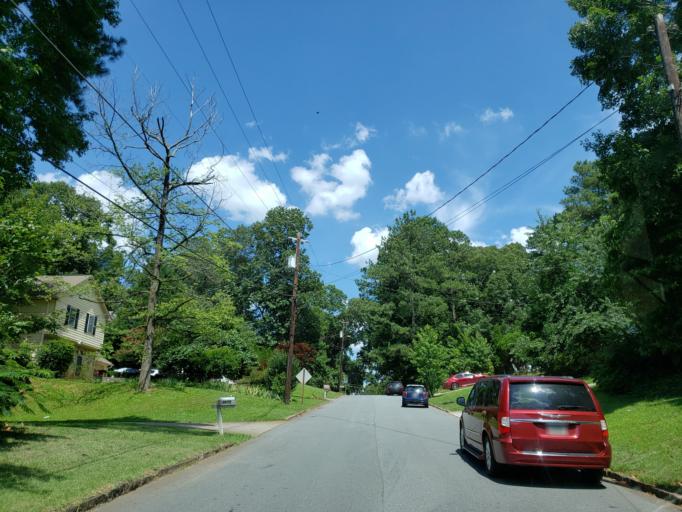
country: US
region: Georgia
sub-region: DeKalb County
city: Doraville
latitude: 33.8971
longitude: -84.2738
